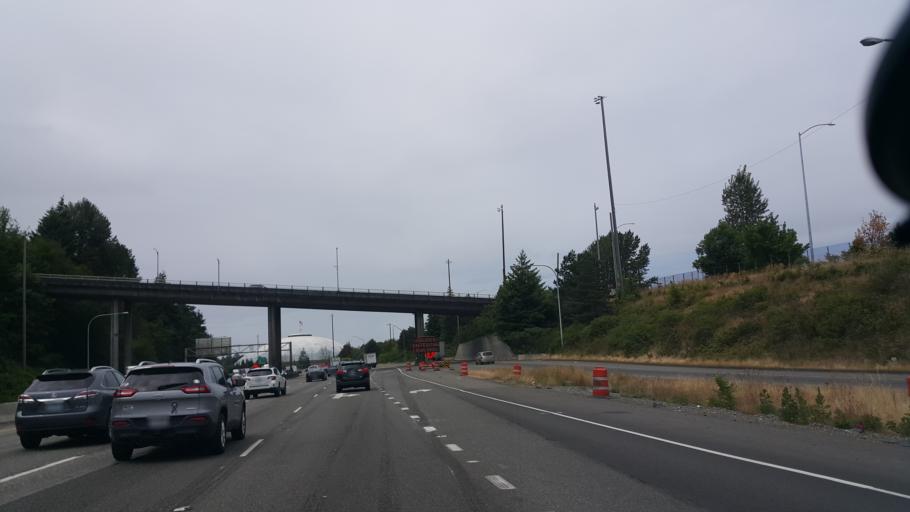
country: US
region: Washington
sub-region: Pierce County
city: Tacoma
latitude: 47.2392
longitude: -122.4140
